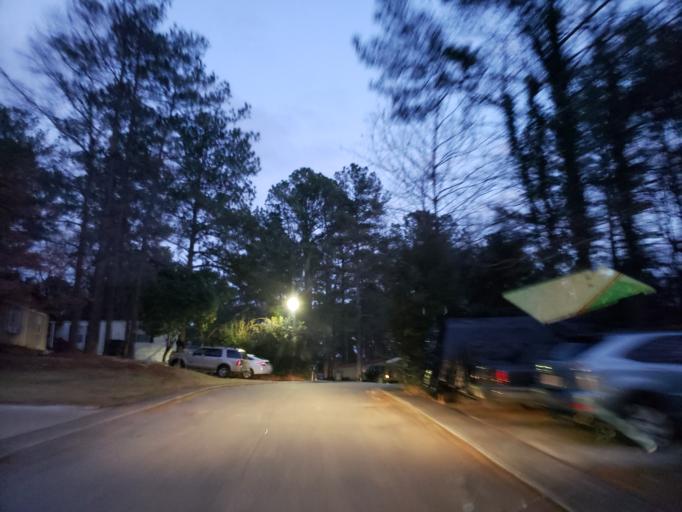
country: US
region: Georgia
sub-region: Cobb County
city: Kennesaw
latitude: 34.0235
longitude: -84.6321
